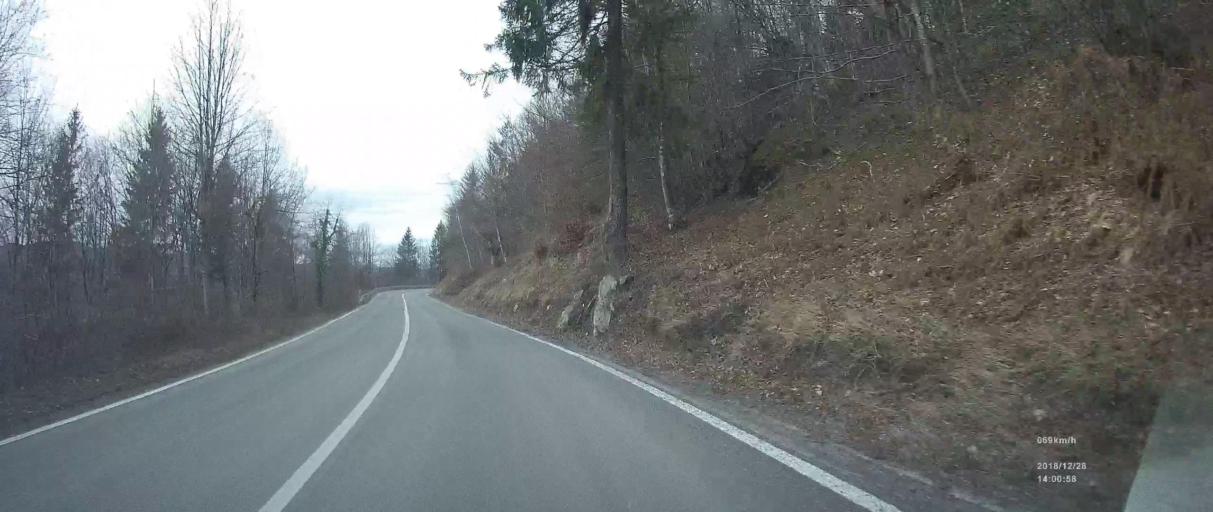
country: SI
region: Kostel
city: Kostel
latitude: 45.4163
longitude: 14.9114
